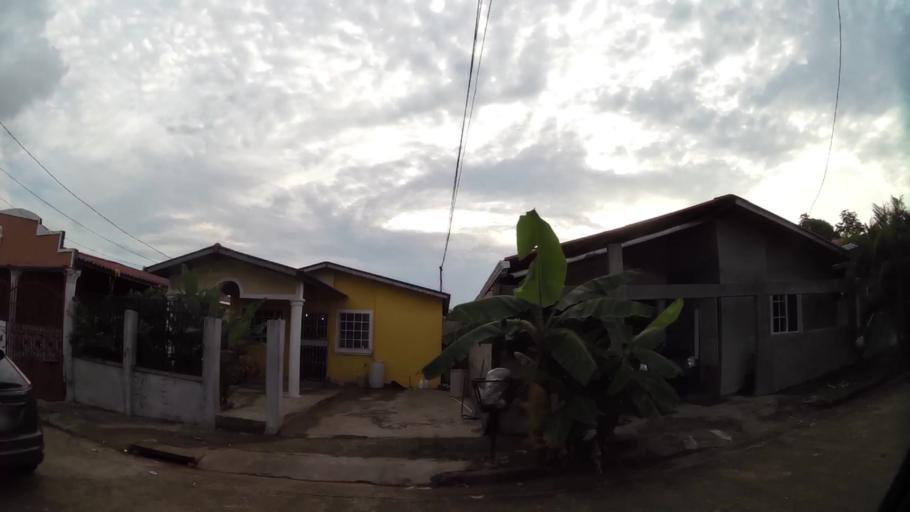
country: PA
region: Panama
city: Tocumen
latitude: 9.0956
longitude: -79.3961
